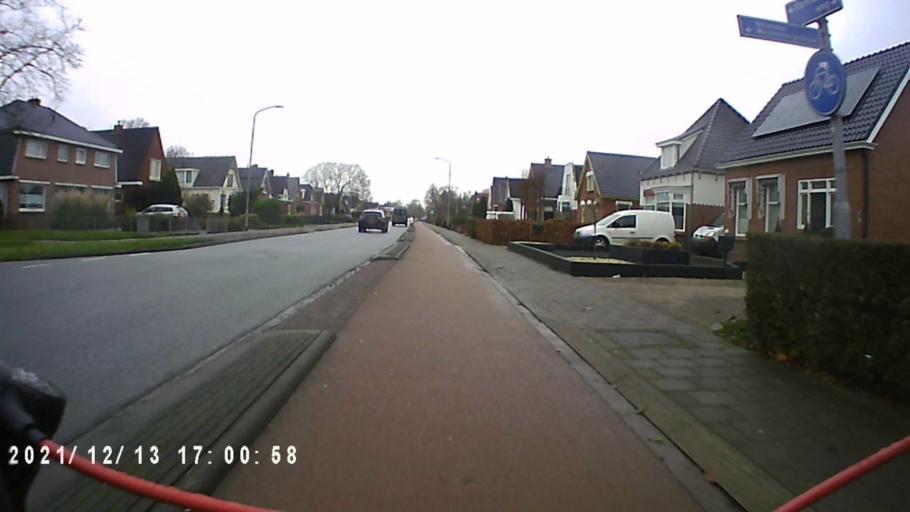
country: NL
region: Groningen
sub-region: Gemeente Appingedam
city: Appingedam
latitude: 53.3200
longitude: 6.8746
